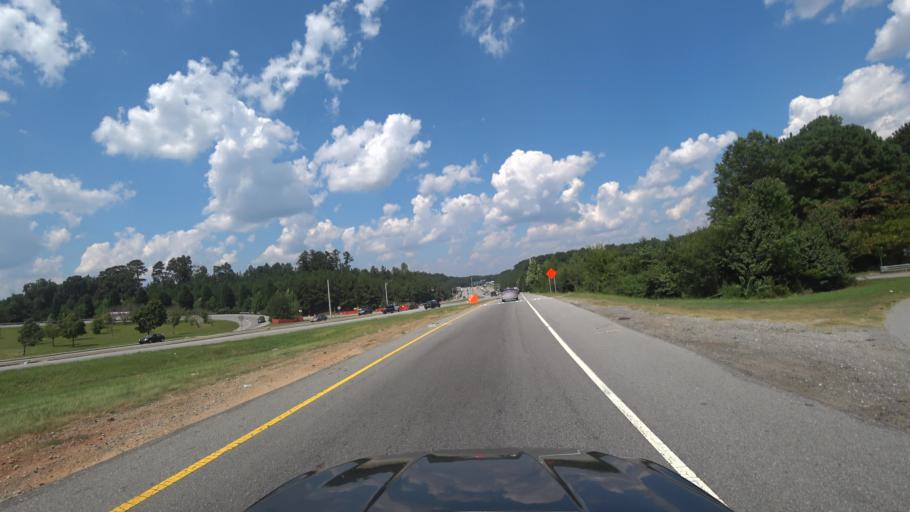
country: US
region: Georgia
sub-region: DeKalb County
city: Doraville
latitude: 33.9130
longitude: -84.2853
